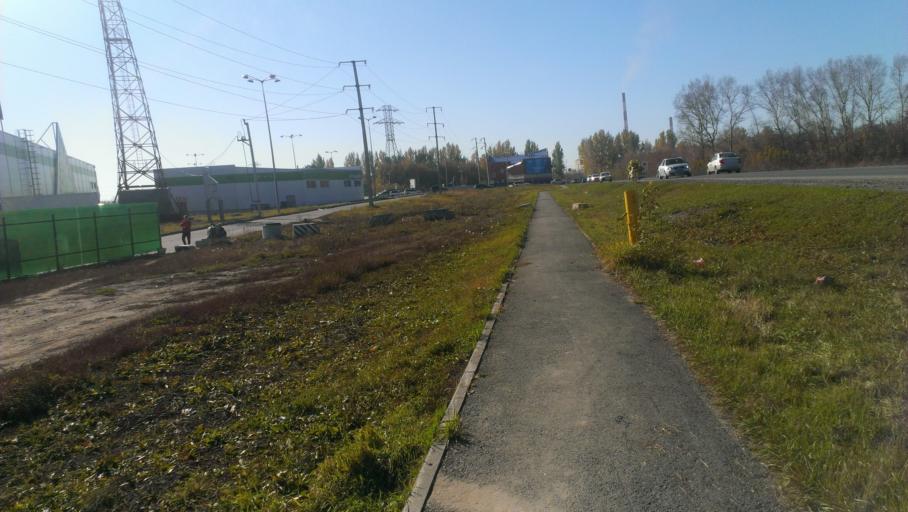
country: RU
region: Altai Krai
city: Novosilikatnyy
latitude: 53.3513
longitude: 83.6314
